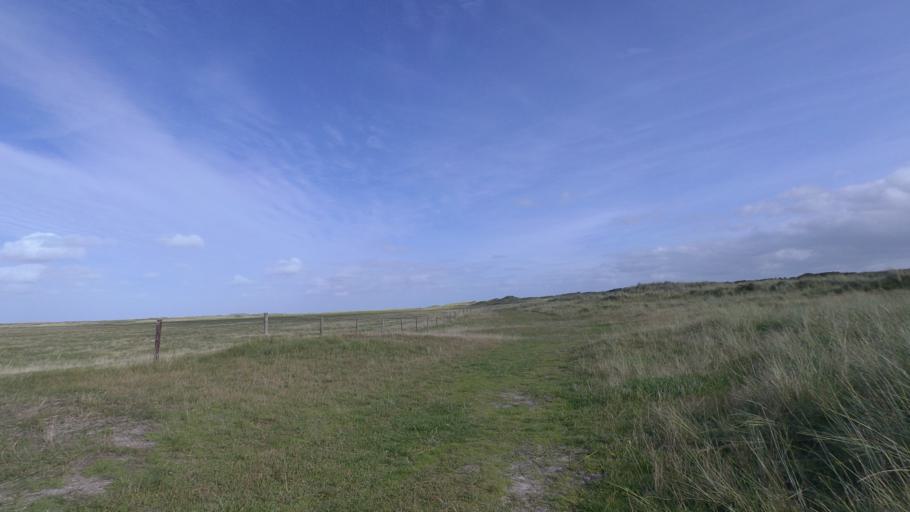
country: NL
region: Friesland
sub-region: Gemeente Ameland
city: Nes
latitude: 53.4517
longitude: 5.8515
